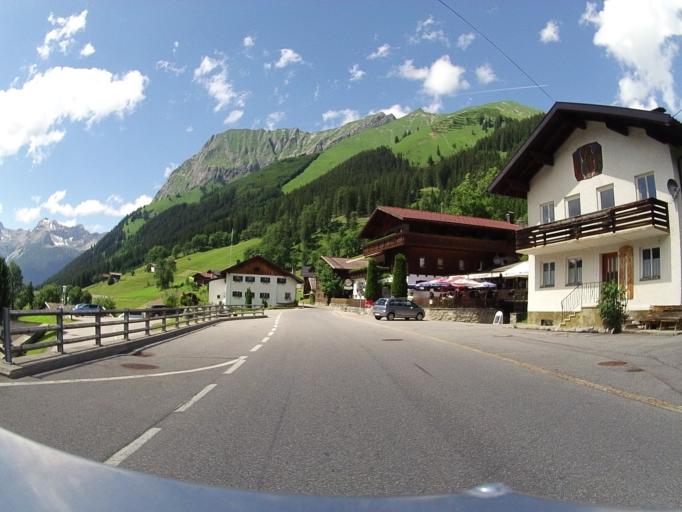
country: AT
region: Tyrol
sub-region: Politischer Bezirk Reutte
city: Elmen
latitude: 47.3079
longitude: 10.5855
